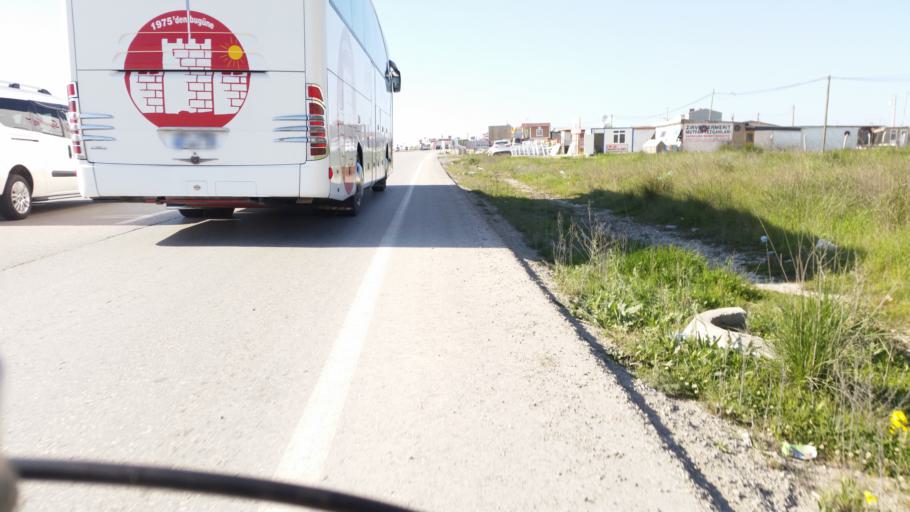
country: TR
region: Tekirdag
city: Cerkezkoey
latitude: 41.3375
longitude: 27.9671
